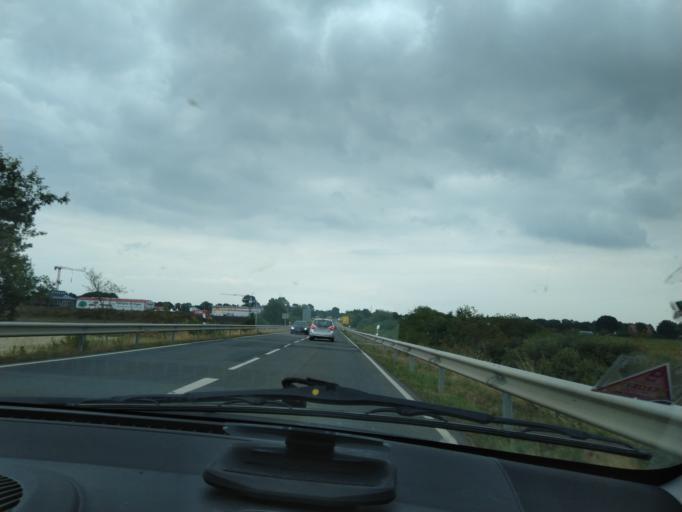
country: DE
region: Lower Saxony
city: Rhede
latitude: 53.0649
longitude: 7.2419
